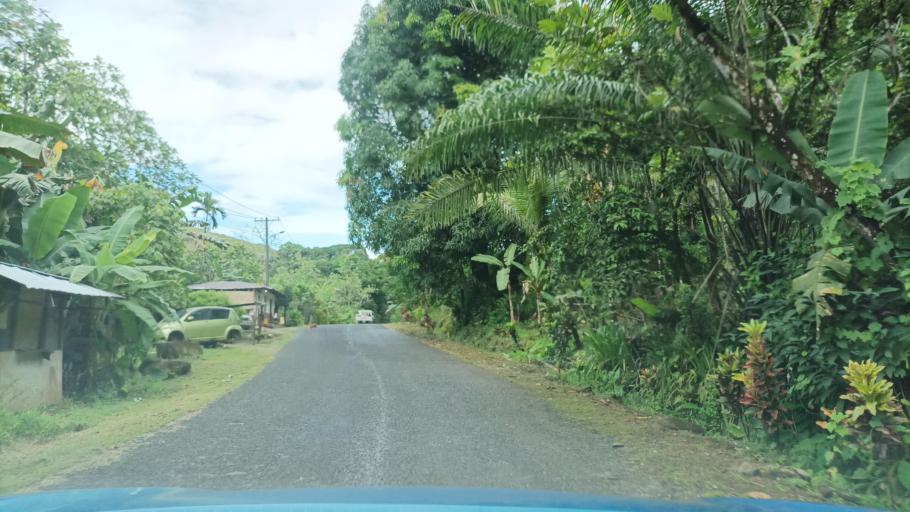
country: FM
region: Pohnpei
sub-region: Sokehs Municipality
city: Palikir - National Government Center
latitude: 6.8455
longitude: 158.1584
